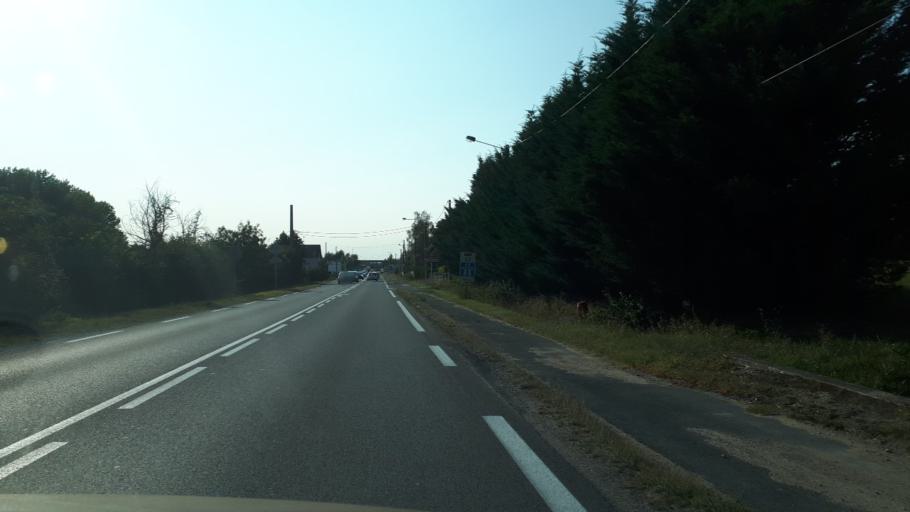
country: FR
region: Centre
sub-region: Departement du Cher
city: Vierzon
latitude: 47.2141
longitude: 2.1238
